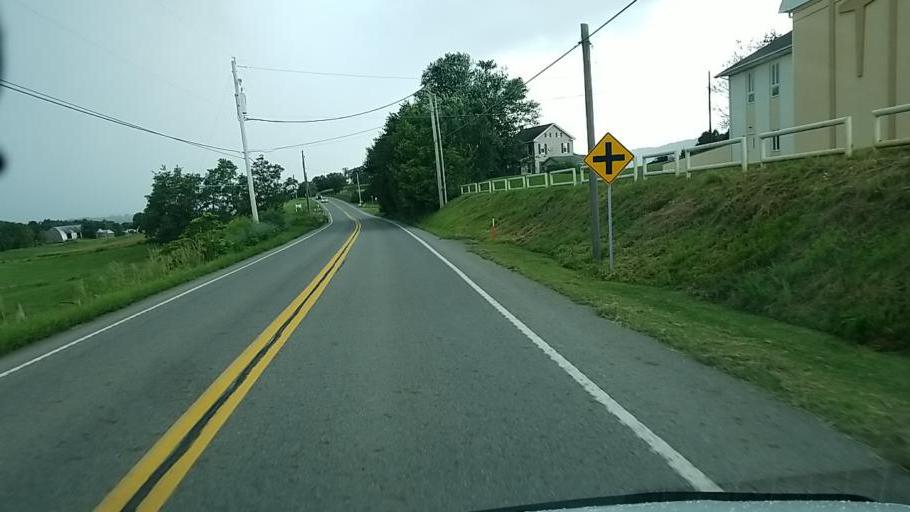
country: US
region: Pennsylvania
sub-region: Dauphin County
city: Elizabethville
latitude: 40.5817
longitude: -76.8745
